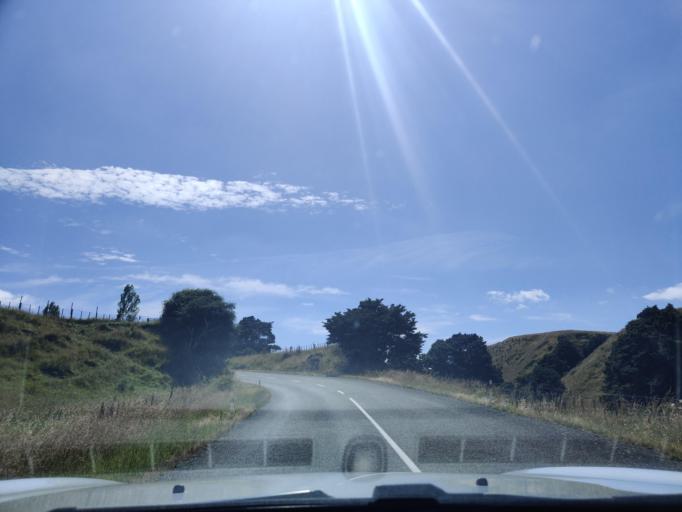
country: NZ
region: Manawatu-Wanganui
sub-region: Rangitikei District
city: Bulls
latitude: -40.1702
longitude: 175.4330
